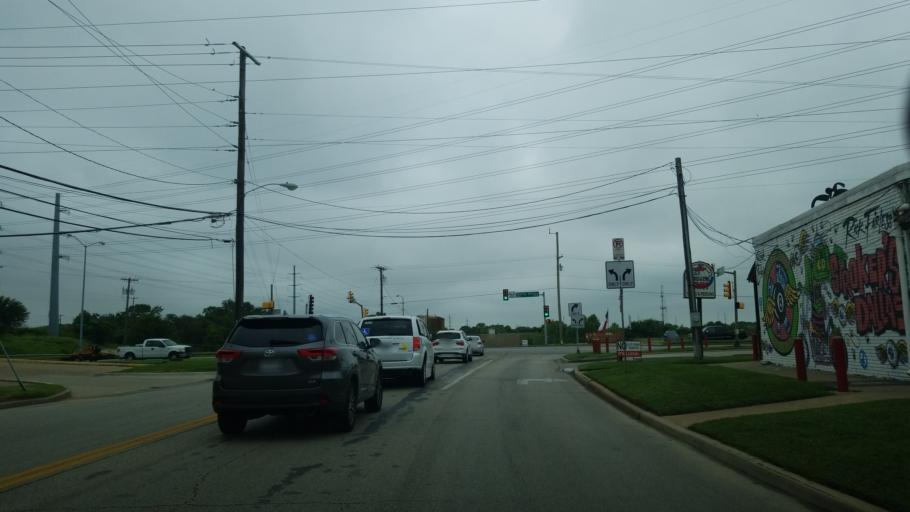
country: US
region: Texas
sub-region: Dallas County
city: University Park
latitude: 32.8419
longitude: -96.8700
